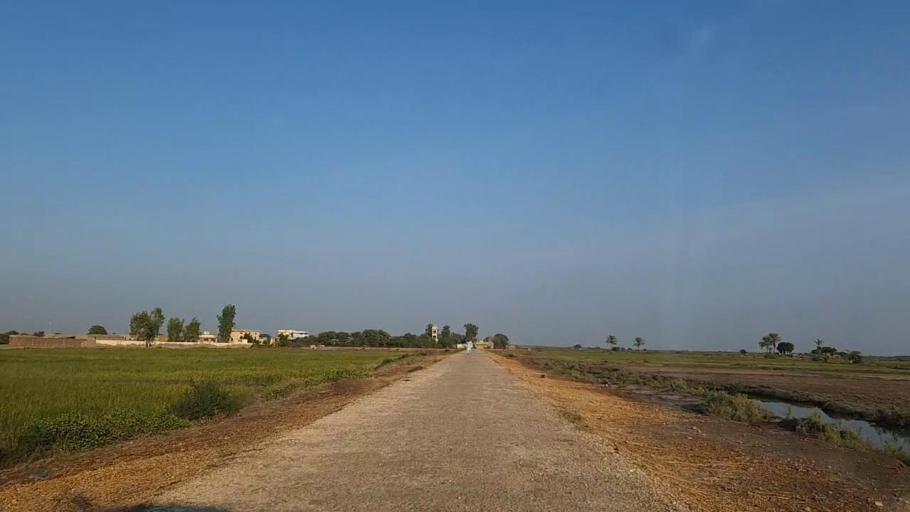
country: PK
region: Sindh
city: Mirpur Batoro
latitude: 24.6074
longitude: 68.0955
